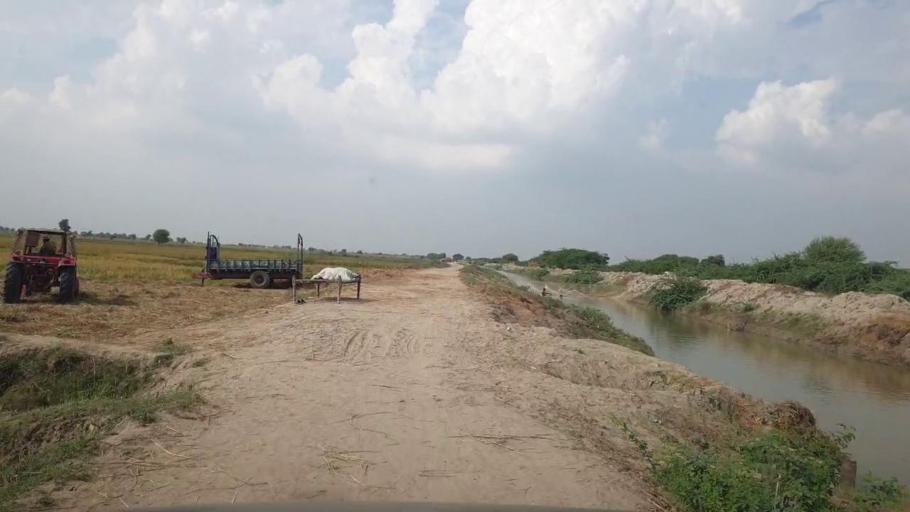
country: PK
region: Sindh
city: Badin
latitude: 24.5678
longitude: 68.6346
